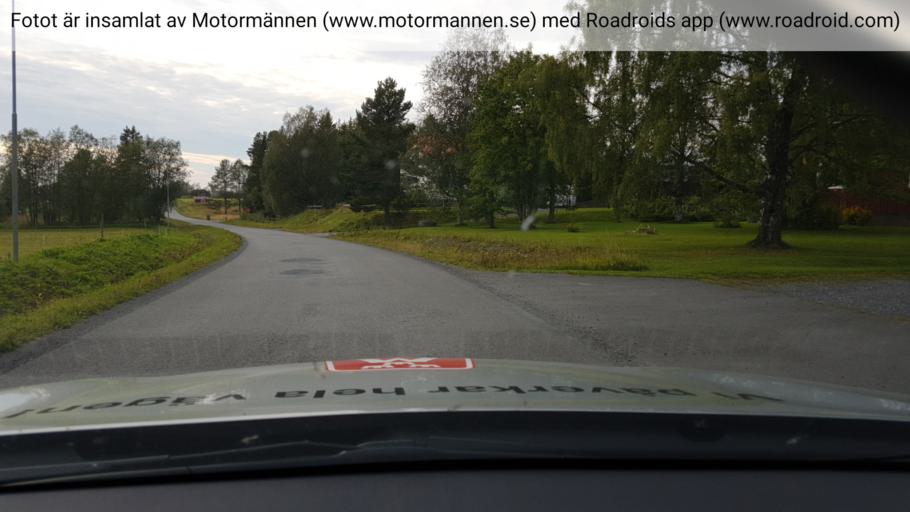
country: SE
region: Jaemtland
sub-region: OEstersunds Kommun
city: Lit
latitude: 63.5649
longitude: 14.9329
